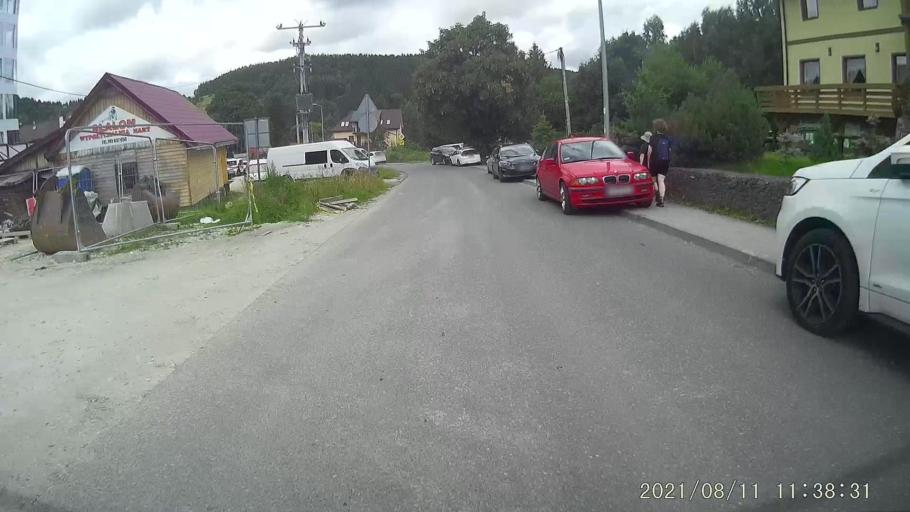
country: PL
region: Lower Silesian Voivodeship
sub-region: Powiat klodzki
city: Stronie Slaskie
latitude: 50.2583
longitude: 16.8250
